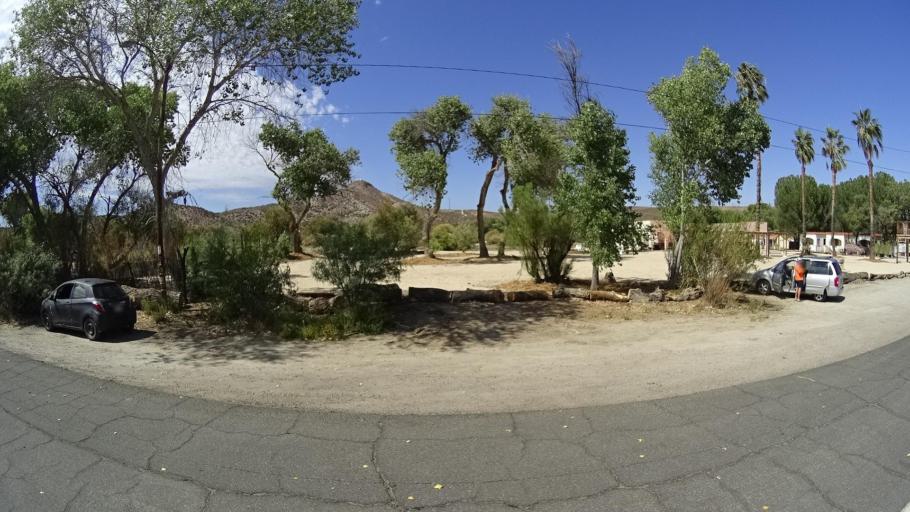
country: MX
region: Baja California
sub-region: Tecate
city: Cereso del Hongo
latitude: 32.6169
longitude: -116.1912
